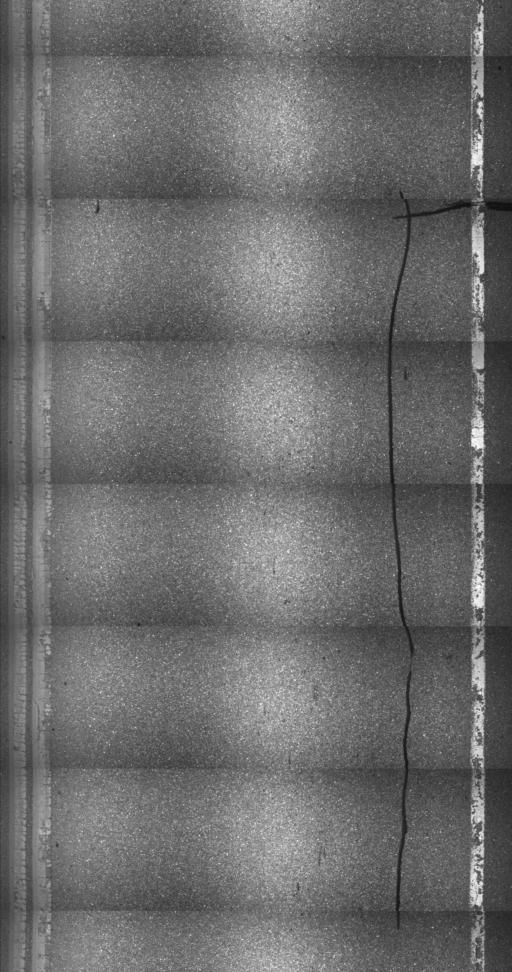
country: US
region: Vermont
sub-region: Chittenden County
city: Milton
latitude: 44.6066
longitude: -73.1575
